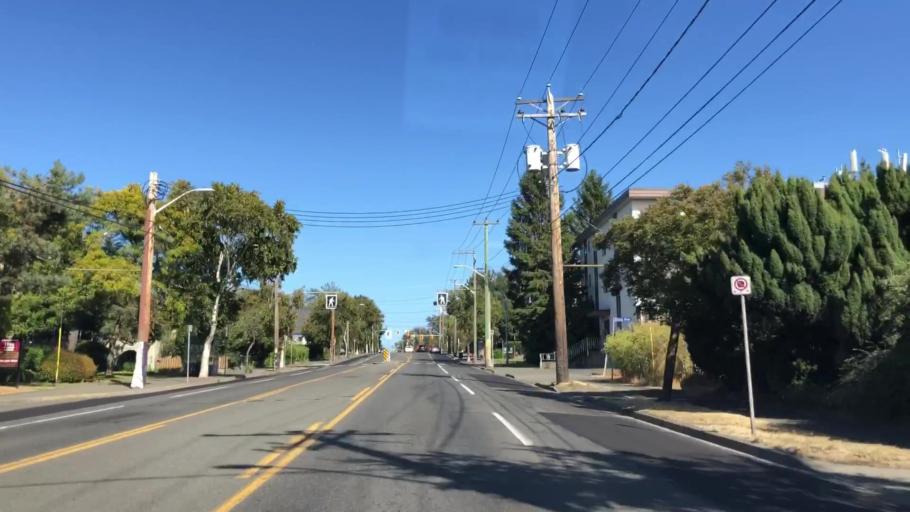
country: CA
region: British Columbia
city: Victoria
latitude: 48.4400
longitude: -123.3550
